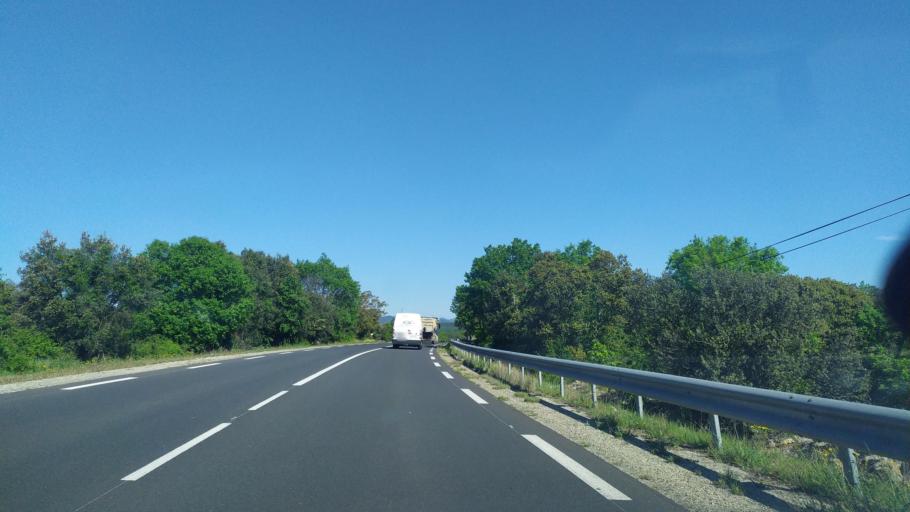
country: FR
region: Languedoc-Roussillon
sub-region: Departement du Gard
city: Quissac
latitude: 43.9236
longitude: 3.9861
